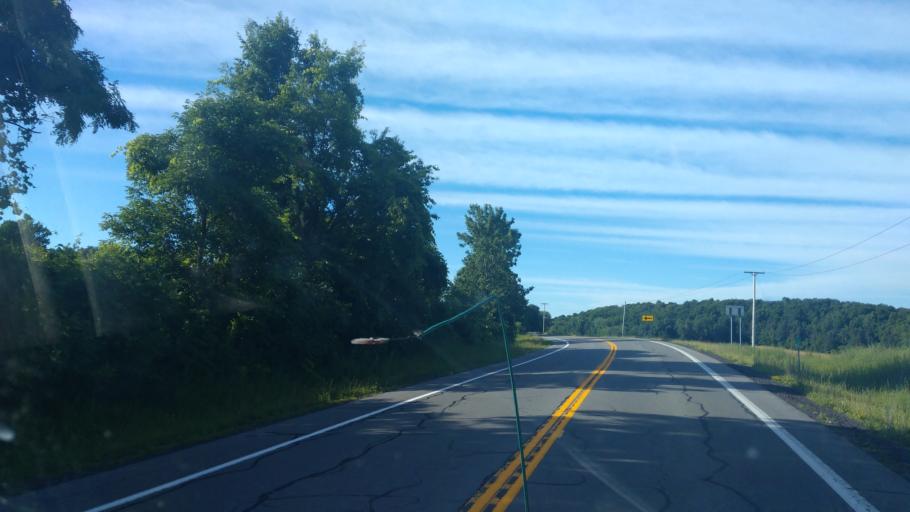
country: US
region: New York
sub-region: Wayne County
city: Lyons
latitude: 43.0938
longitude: -76.9846
